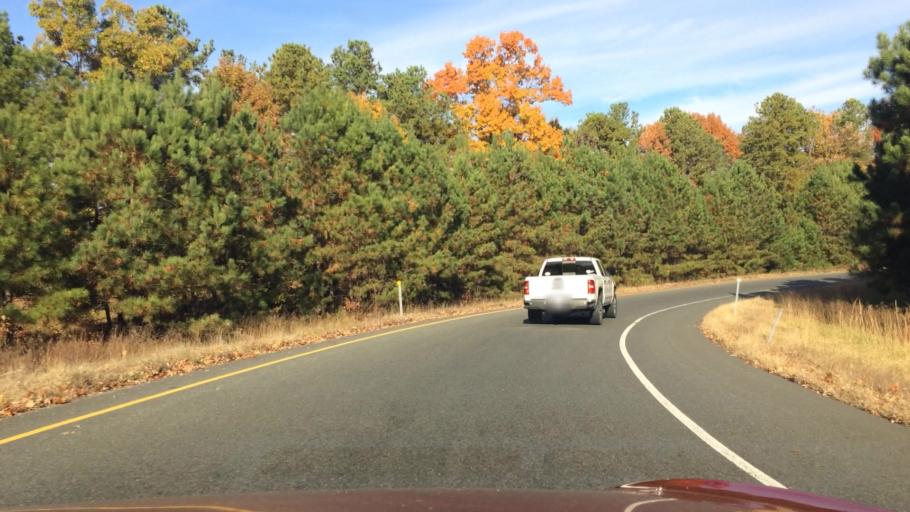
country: US
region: Virginia
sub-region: Henrico County
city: Short Pump
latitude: 37.6543
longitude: -77.6079
